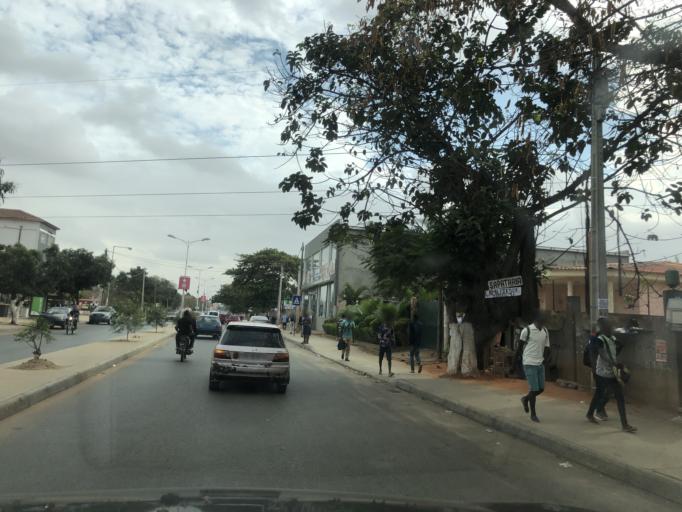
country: AO
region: Luanda
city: Luanda
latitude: -8.9110
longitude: 13.3718
